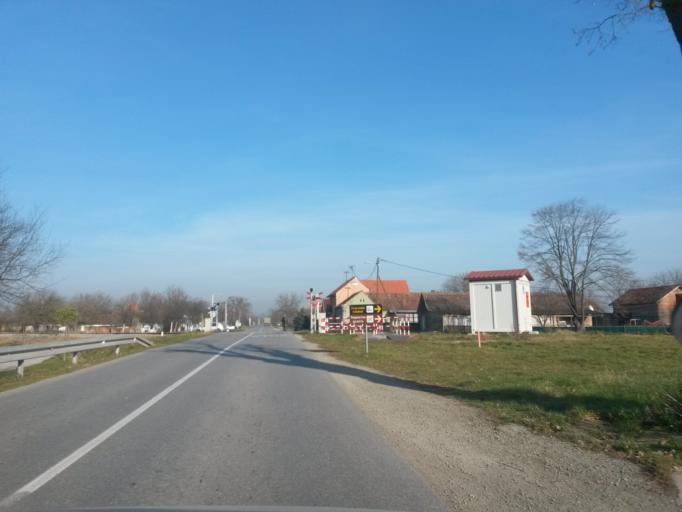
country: HR
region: Vukovarsko-Srijemska
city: Privlaka
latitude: 45.2019
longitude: 18.8470
